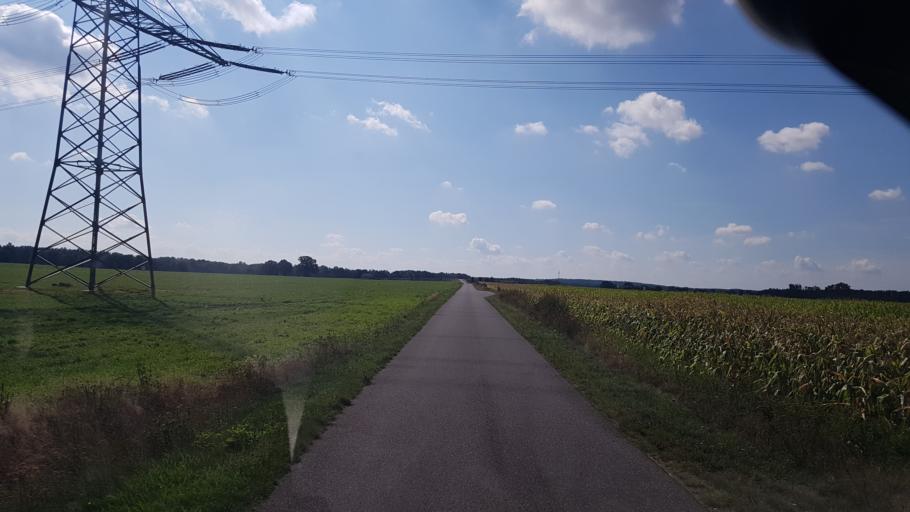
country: DE
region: Brandenburg
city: Drebkau
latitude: 51.6595
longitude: 14.2459
